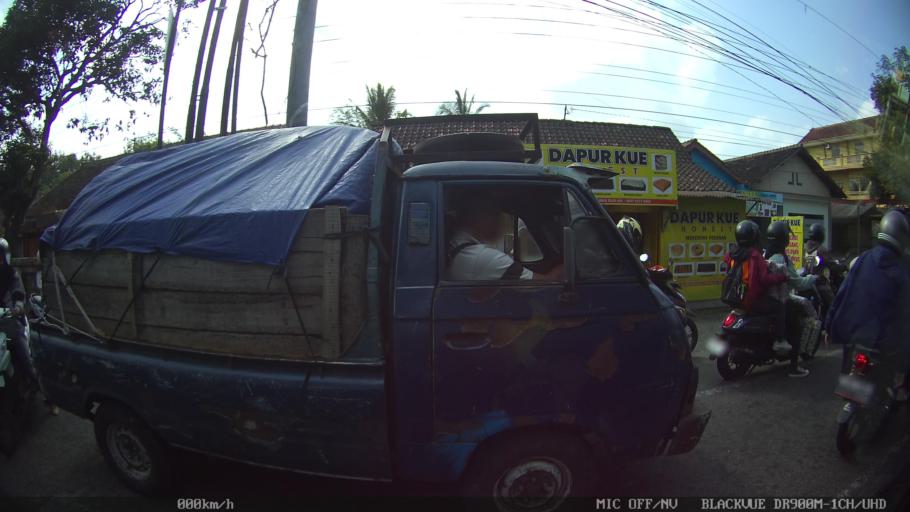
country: ID
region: Daerah Istimewa Yogyakarta
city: Srandakan
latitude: -7.8445
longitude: 110.2183
